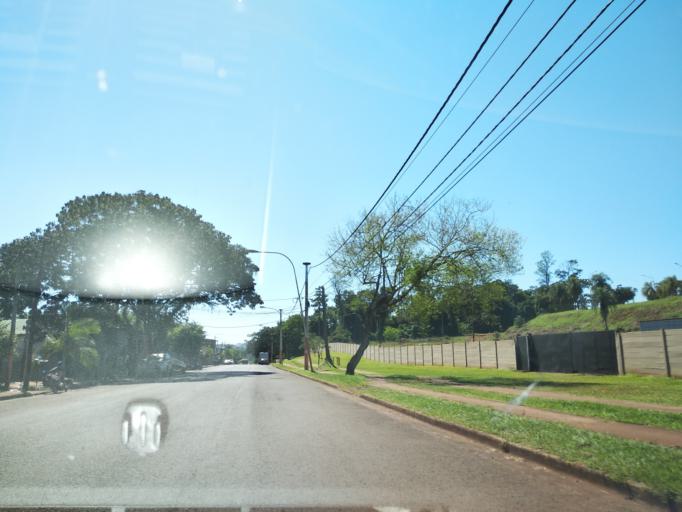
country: AR
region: Misiones
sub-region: Departamento de Iguazu
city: Puerto Iguazu
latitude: -25.6004
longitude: -54.5670
